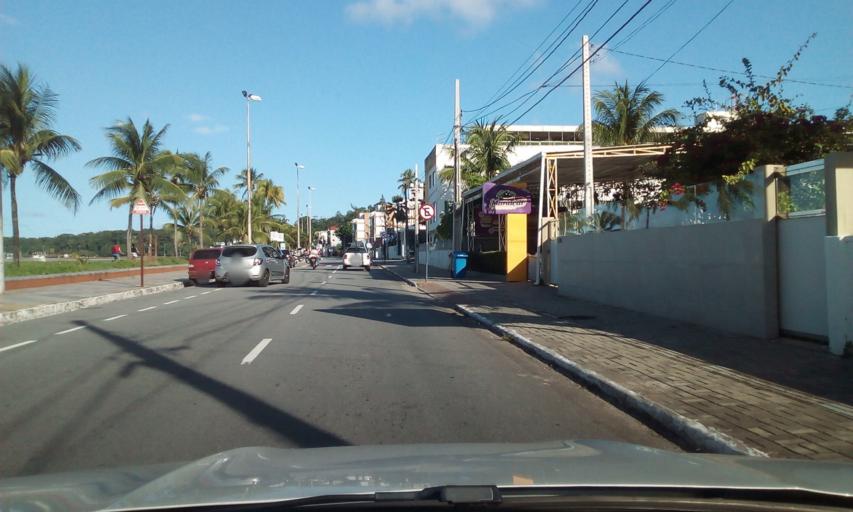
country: BR
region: Paraiba
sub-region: Joao Pessoa
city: Joao Pessoa
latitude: -7.1415
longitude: -34.8153
